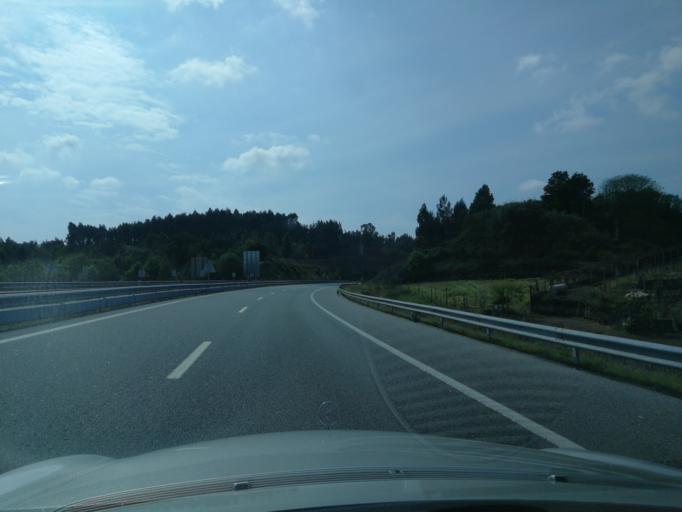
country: PT
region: Braga
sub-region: Vila Nova de Famalicao
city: Calendario
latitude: 41.3819
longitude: -8.5261
